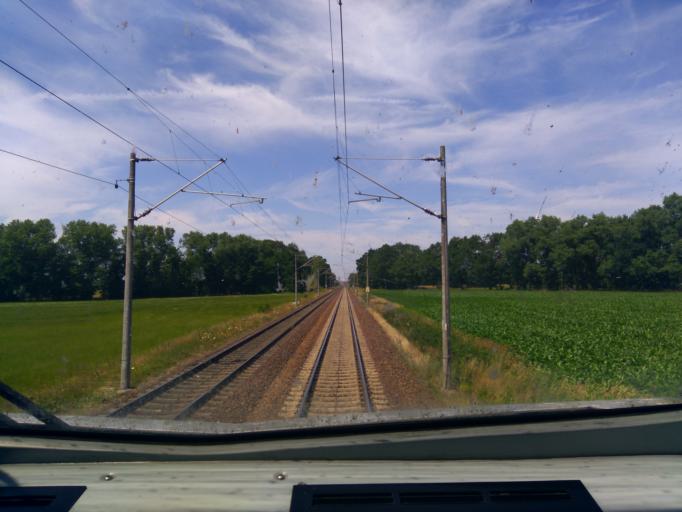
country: DE
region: Brandenburg
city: Dreetz
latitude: 52.8347
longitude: 12.4777
